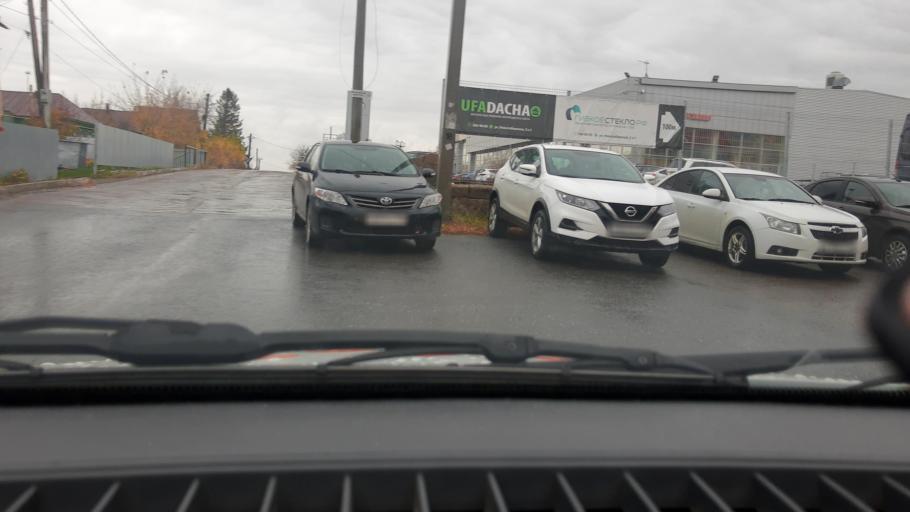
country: RU
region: Bashkortostan
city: Ufa
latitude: 54.7526
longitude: 55.9749
